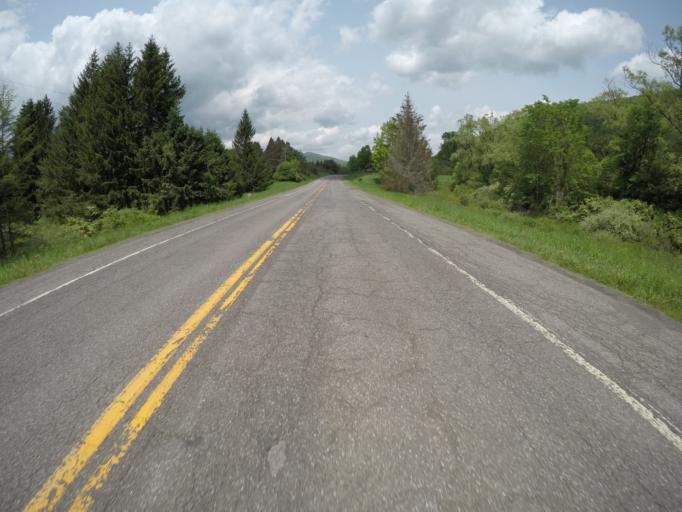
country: US
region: New York
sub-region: Delaware County
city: Stamford
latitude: 42.2513
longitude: -74.5953
